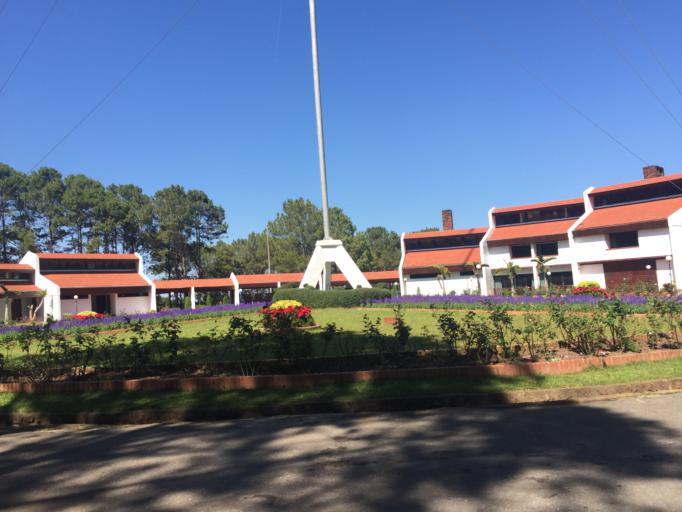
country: TH
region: Phetchabun
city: Khao Kho
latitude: 16.5529
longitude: 100.9760
